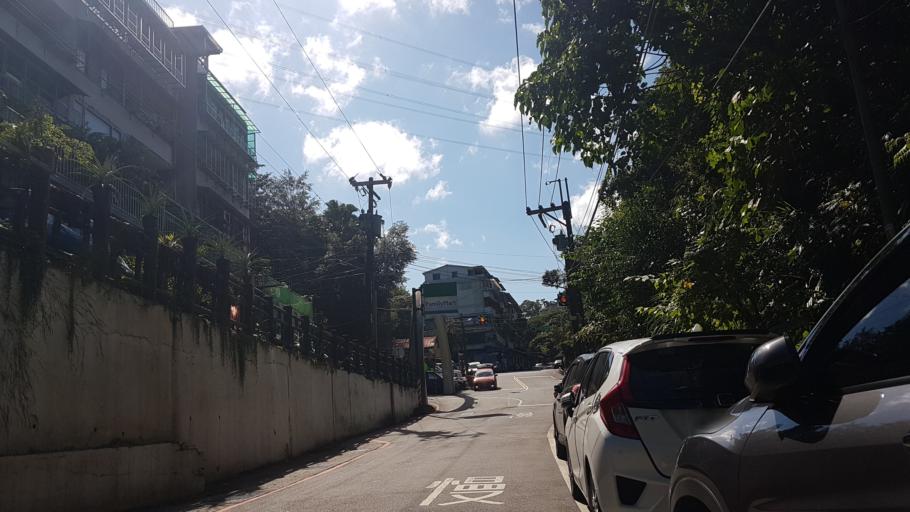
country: TW
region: Taipei
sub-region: Taipei
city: Banqiao
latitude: 24.9498
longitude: 121.5299
